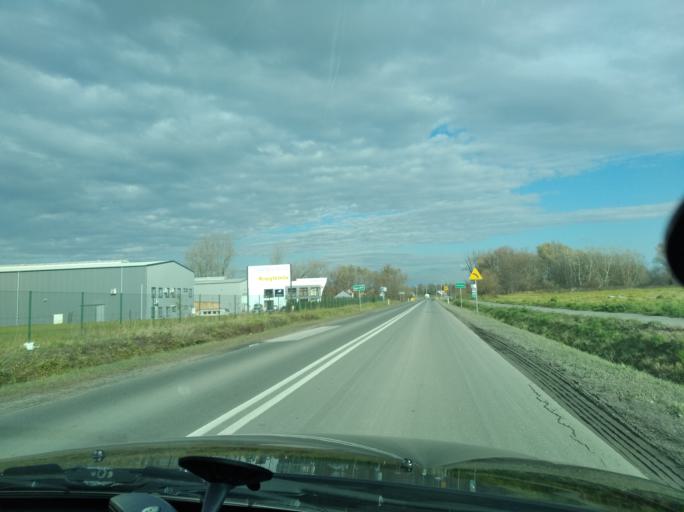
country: PL
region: Subcarpathian Voivodeship
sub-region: Powiat ropczycko-sedziszowski
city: Ostrow
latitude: 50.0874
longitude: 21.5894
